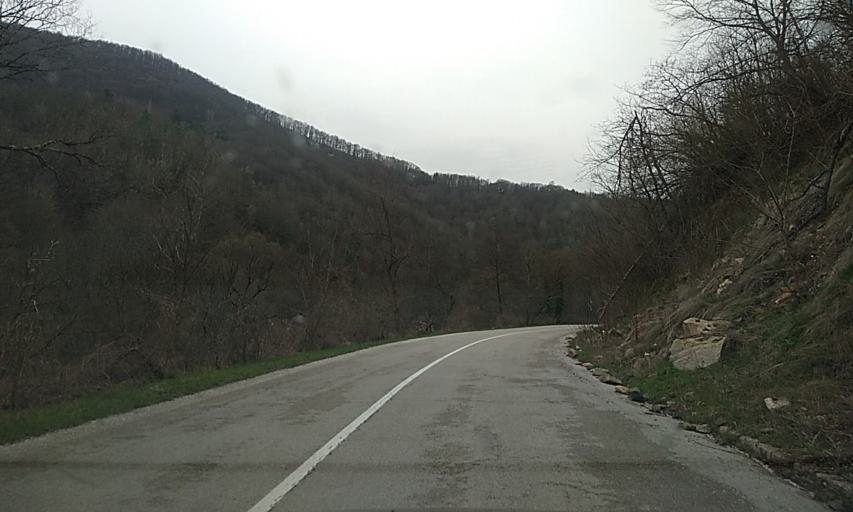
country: RS
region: Central Serbia
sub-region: Pcinjski Okrug
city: Bosilegrad
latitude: 42.4025
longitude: 22.4677
